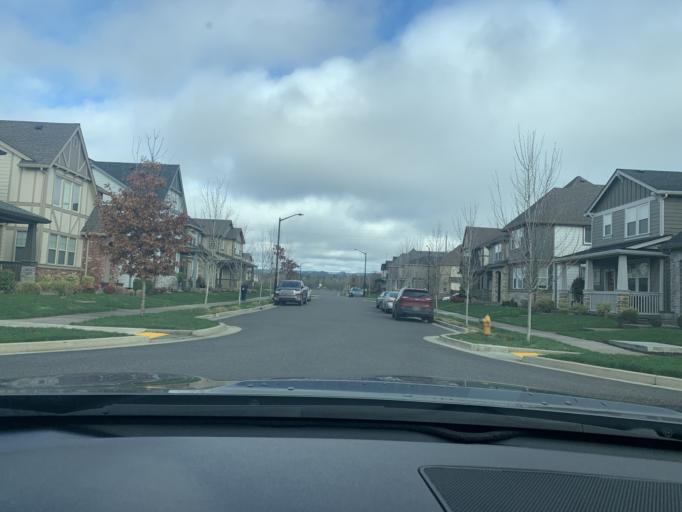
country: US
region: Oregon
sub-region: Washington County
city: North Plains
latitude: 45.5949
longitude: -122.9743
